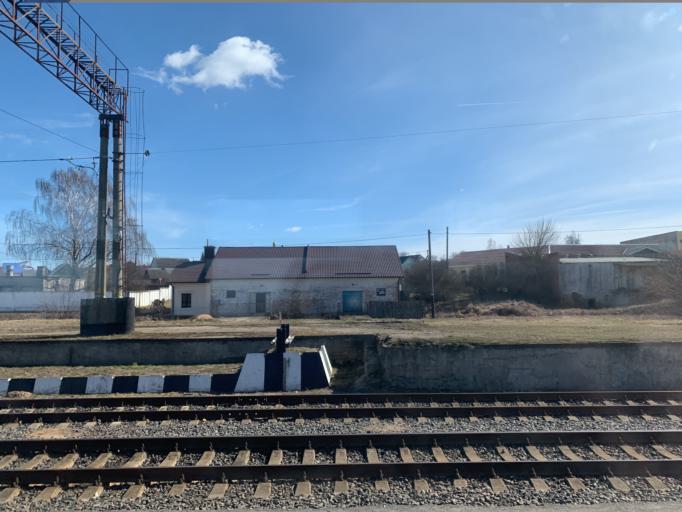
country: BY
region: Minsk
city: Haradzyeya
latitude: 53.3153
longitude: 26.5387
